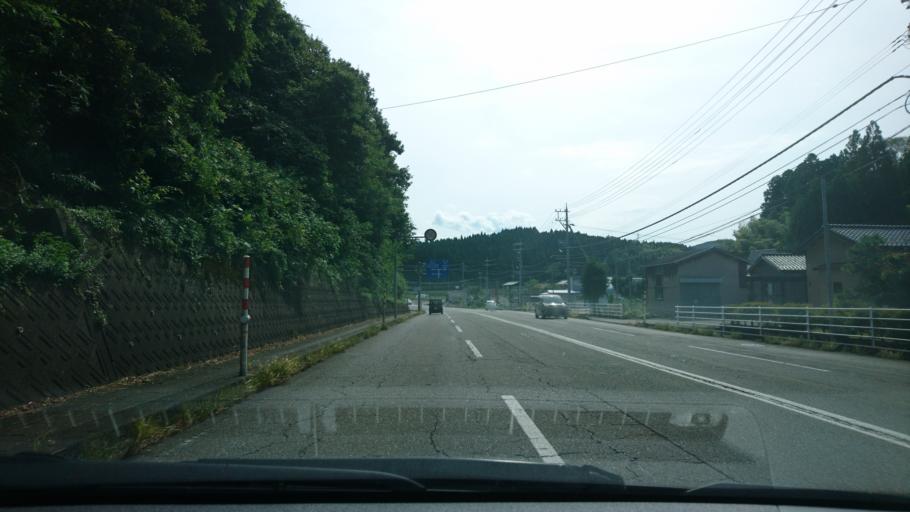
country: JP
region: Fukui
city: Maruoka
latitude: 36.2909
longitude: 136.2943
